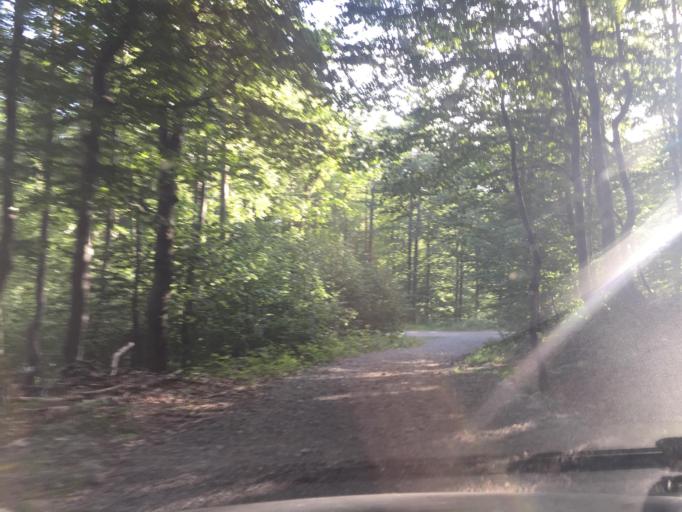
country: HR
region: Primorsko-Goranska
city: Podhum
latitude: 45.4328
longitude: 14.5791
